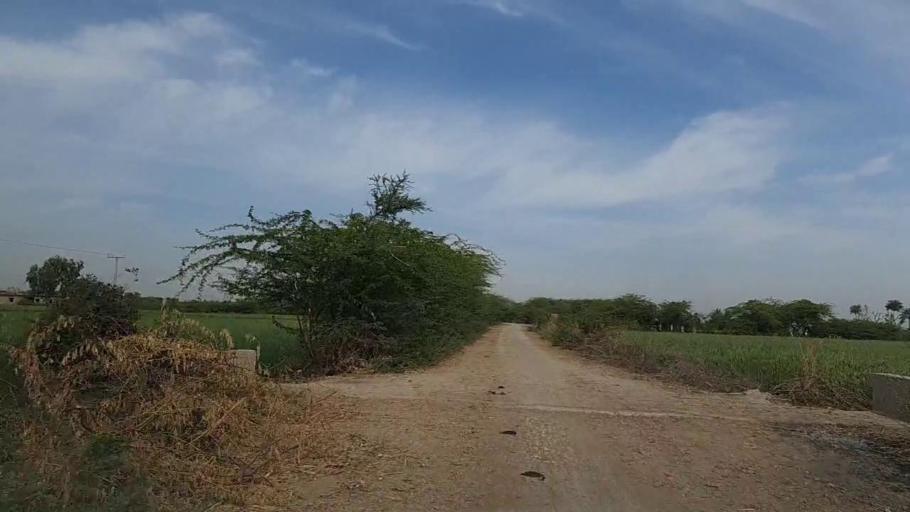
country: PK
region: Sindh
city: Samaro
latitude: 25.2987
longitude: 69.4239
